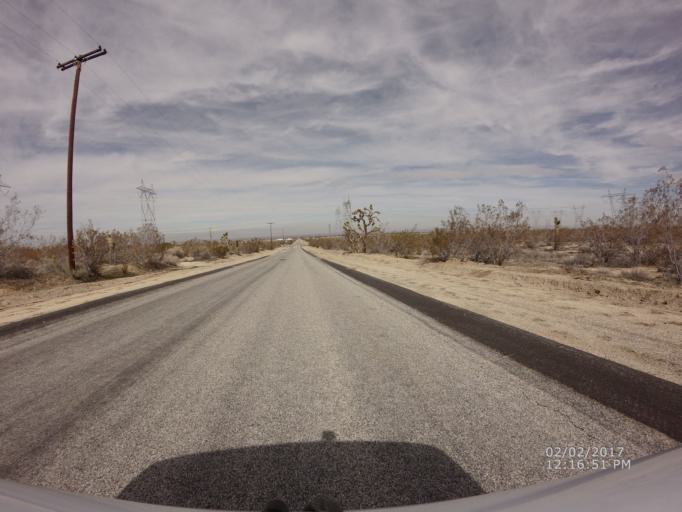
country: US
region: California
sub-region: Los Angeles County
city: Littlerock
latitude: 34.5085
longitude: -117.9749
